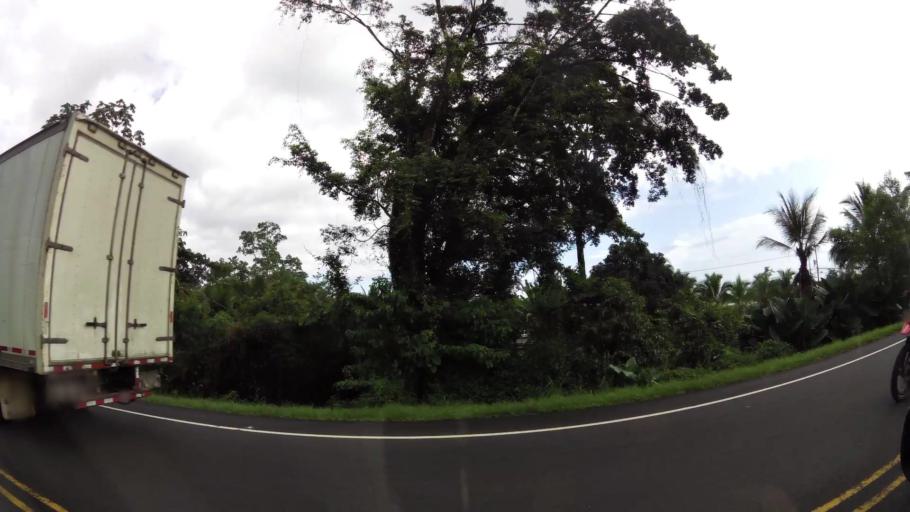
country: CR
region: Limon
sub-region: Canton de Guacimo
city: Guacimo
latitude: 10.2092
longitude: -83.6979
